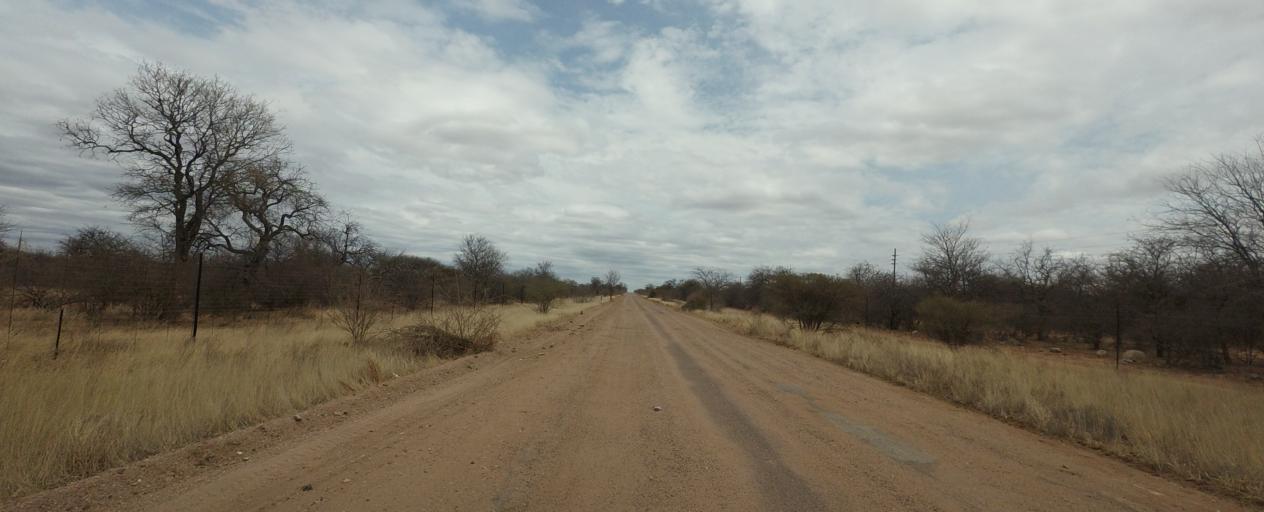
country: BW
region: Central
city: Mathathane
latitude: -22.6689
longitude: 28.6876
